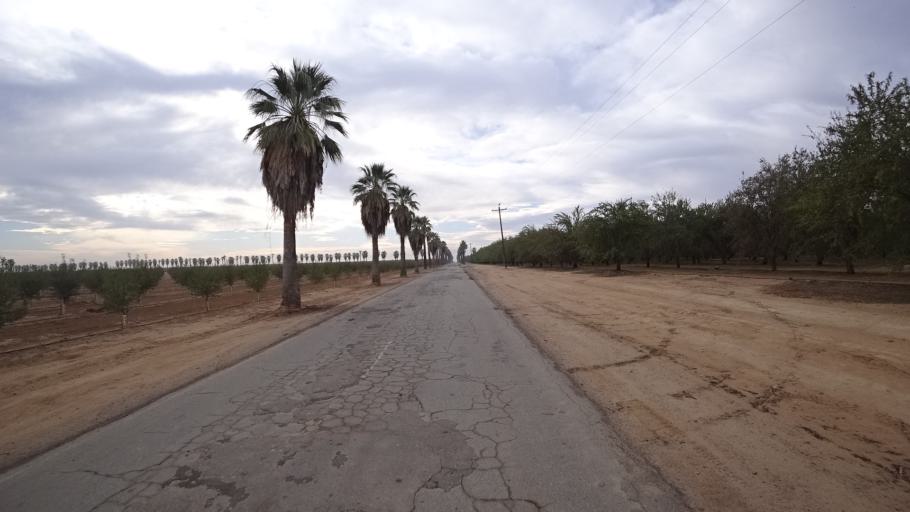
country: US
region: California
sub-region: Kern County
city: Rosedale
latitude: 35.4373
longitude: -119.1721
